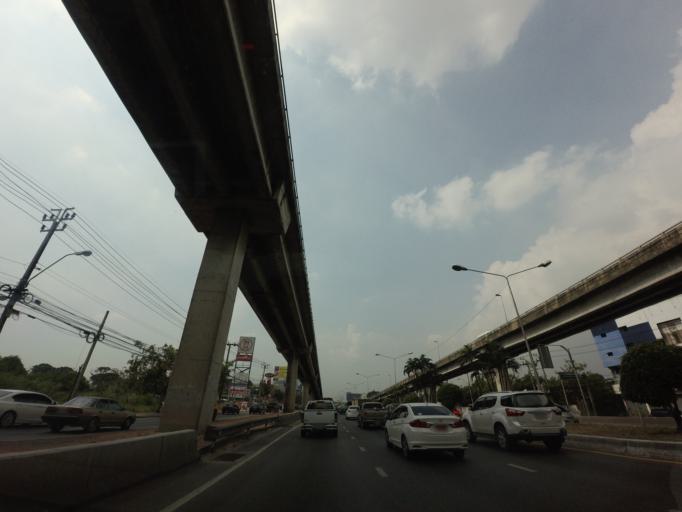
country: TH
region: Bangkok
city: Thawi Watthana
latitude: 13.7851
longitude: 100.3772
